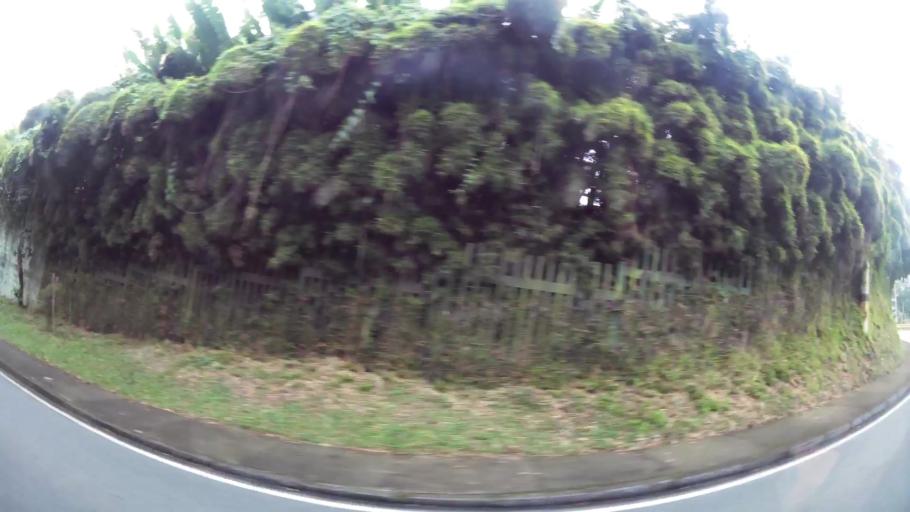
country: CO
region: Antioquia
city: Envigado
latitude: 6.1925
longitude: -75.5580
